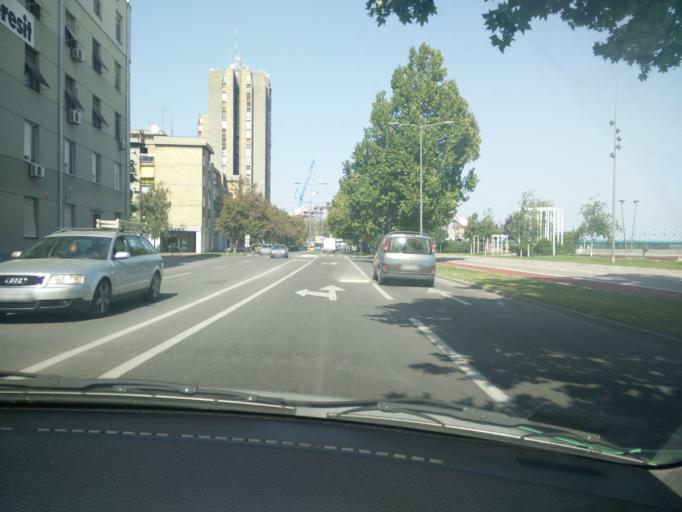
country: RS
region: Autonomna Pokrajina Vojvodina
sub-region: Juznobacki Okrug
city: Novi Sad
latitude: 45.2588
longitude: 19.8551
